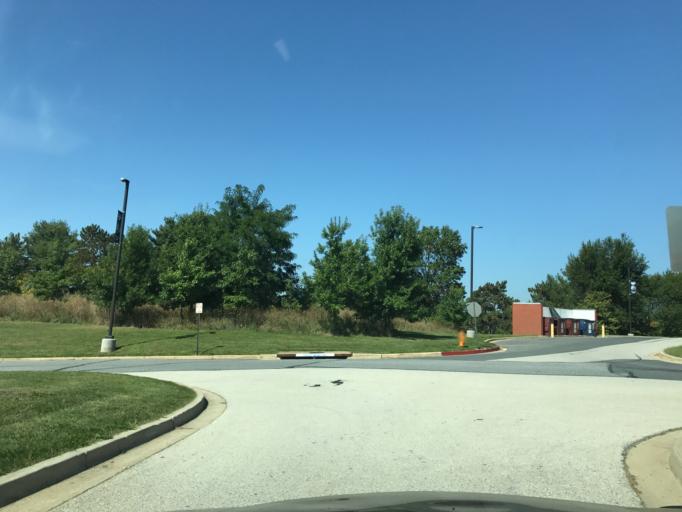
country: US
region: Maryland
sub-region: Howard County
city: Columbia
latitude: 39.2263
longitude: -76.8137
